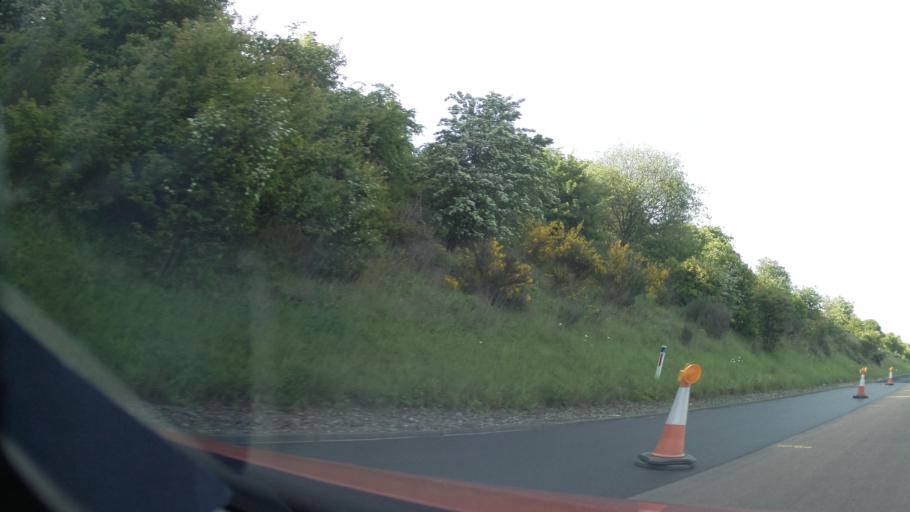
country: GB
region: Scotland
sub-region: Fife
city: Crossgates
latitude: 56.0951
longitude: -3.3981
